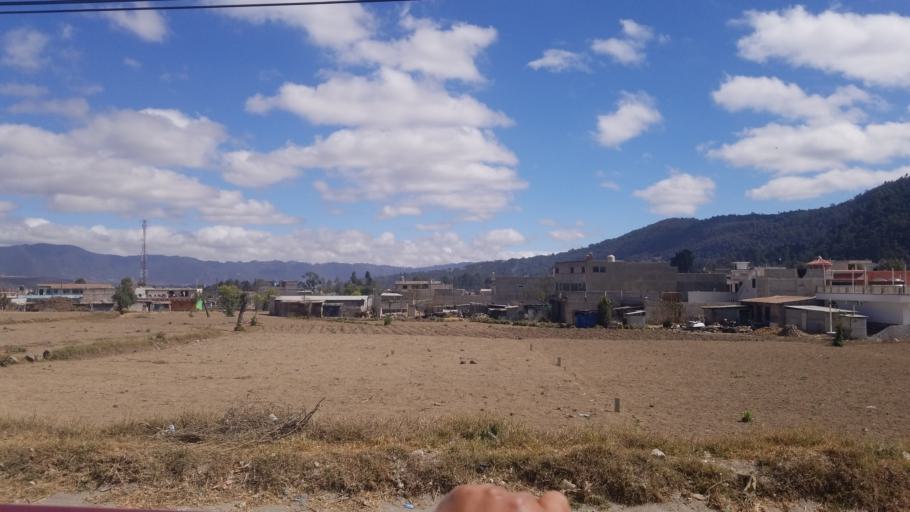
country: GT
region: Quetzaltenango
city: Almolonga
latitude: 14.7898
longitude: -91.5423
